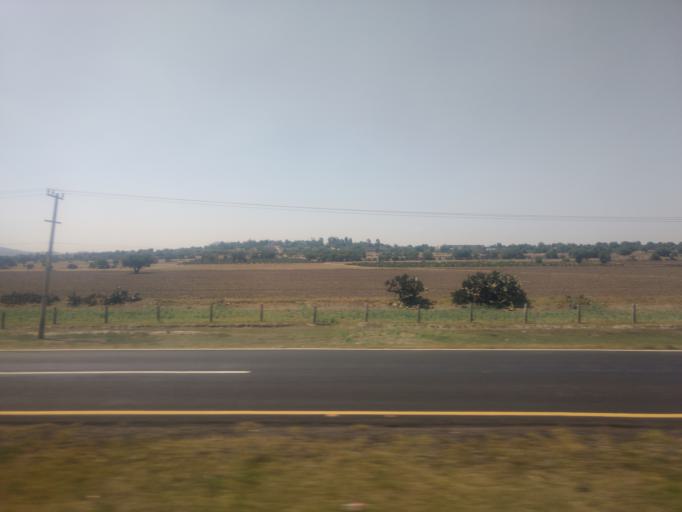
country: MX
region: Morelos
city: Nopaltepec
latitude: 19.7735
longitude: -98.7420
